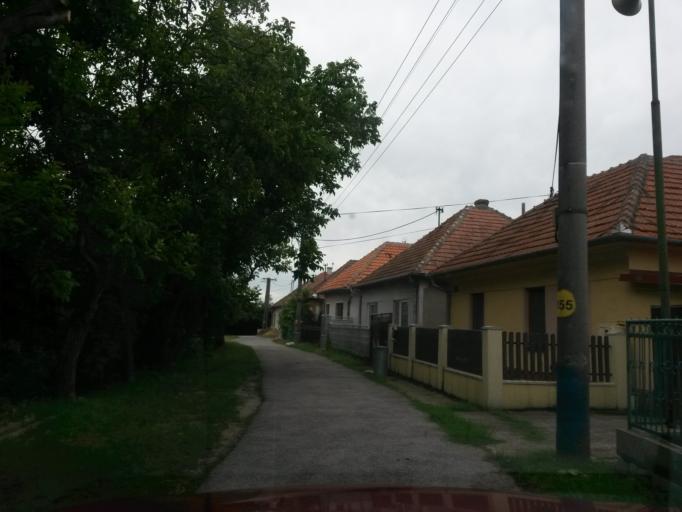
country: SK
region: Nitriansky
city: Surany
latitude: 48.1103
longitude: 18.2372
